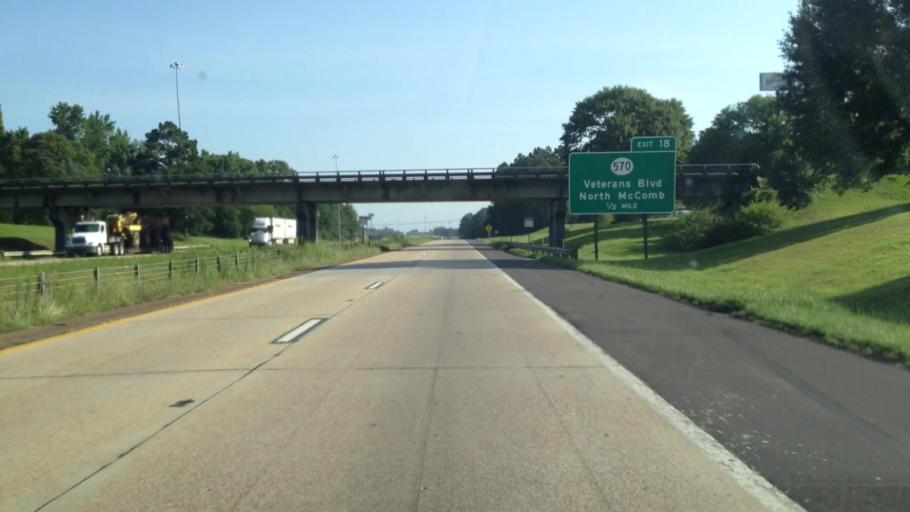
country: US
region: Mississippi
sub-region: Pike County
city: McComb
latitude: 31.2469
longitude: -90.4800
